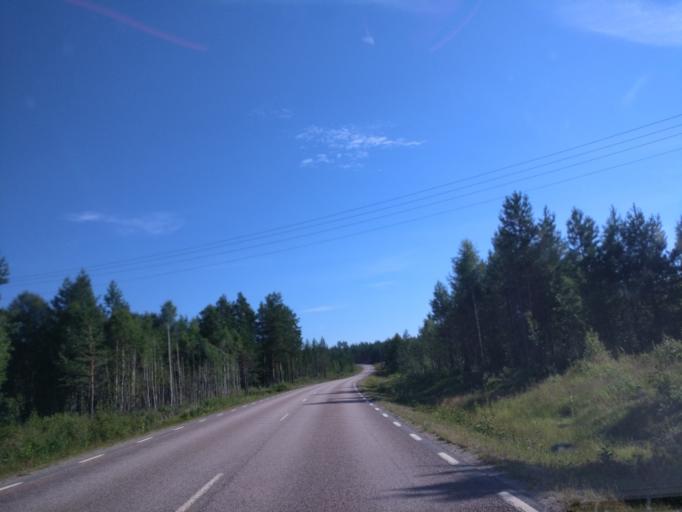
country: SE
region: Vaermland
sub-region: Hagfors Kommun
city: Hagfors
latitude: 60.0271
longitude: 13.9084
